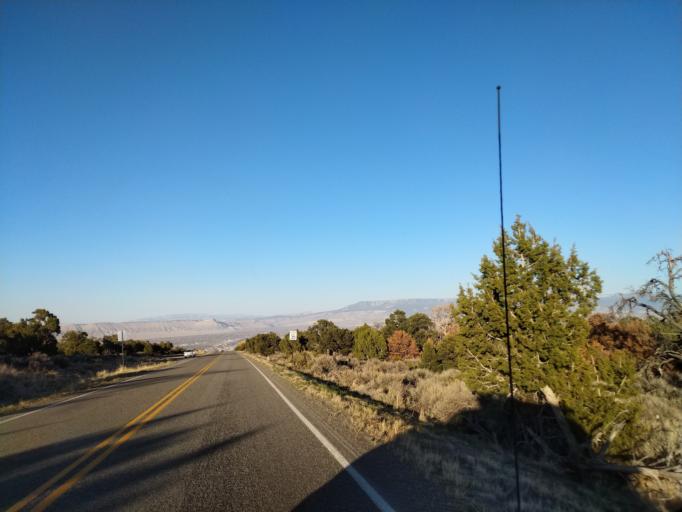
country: US
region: Colorado
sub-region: Mesa County
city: Redlands
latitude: 39.0173
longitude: -108.6631
